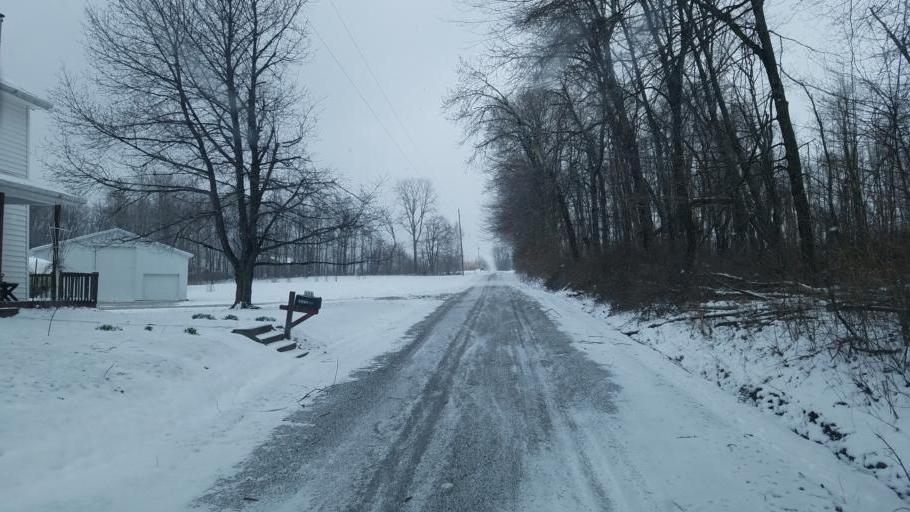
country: US
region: Pennsylvania
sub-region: Crawford County
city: Cochranton
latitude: 41.4444
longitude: -79.9888
